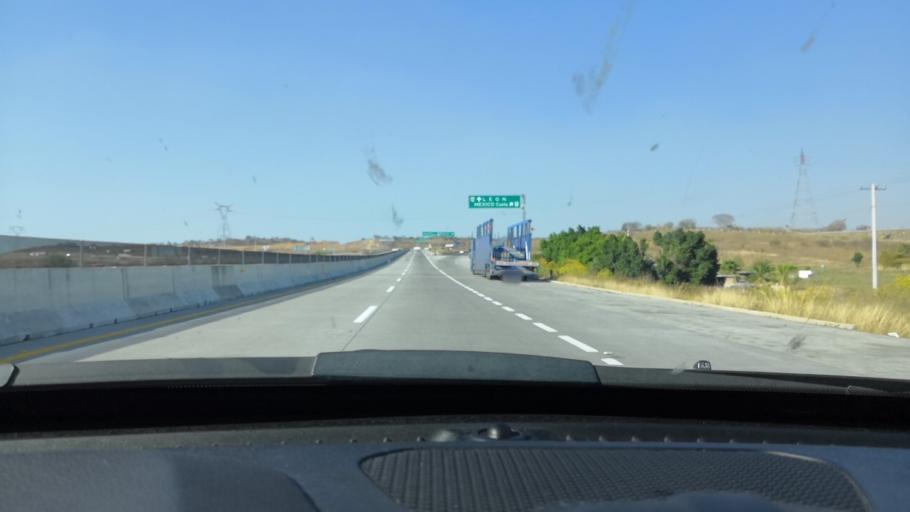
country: MX
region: Jalisco
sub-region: Zapotlanejo
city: La Mezquitera
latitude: 20.5811
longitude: -103.1000
